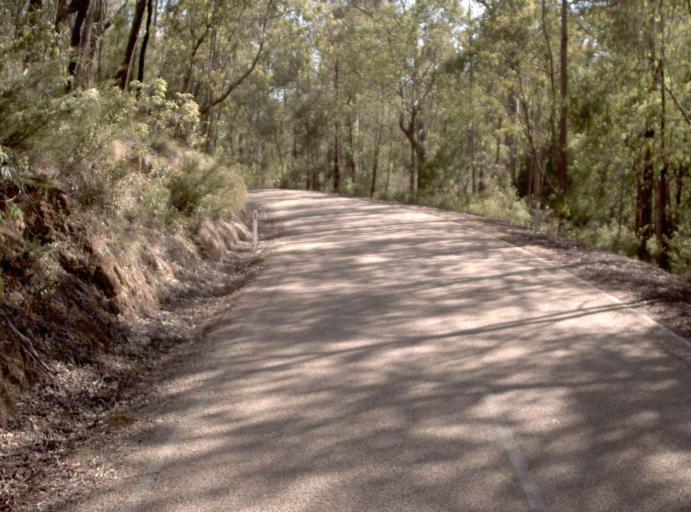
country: AU
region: Victoria
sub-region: East Gippsland
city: Lakes Entrance
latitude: -37.4996
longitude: 148.5512
